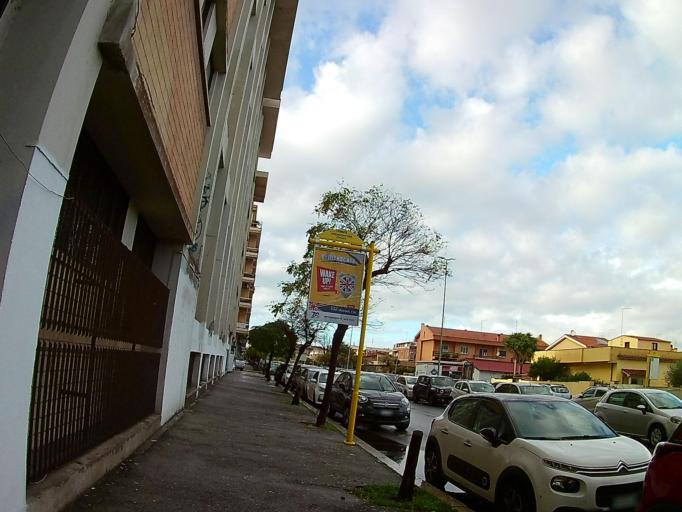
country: IT
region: Latium
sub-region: Citta metropolitana di Roma Capitale
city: Lido di Ostia
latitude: 41.7375
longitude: 12.2915
